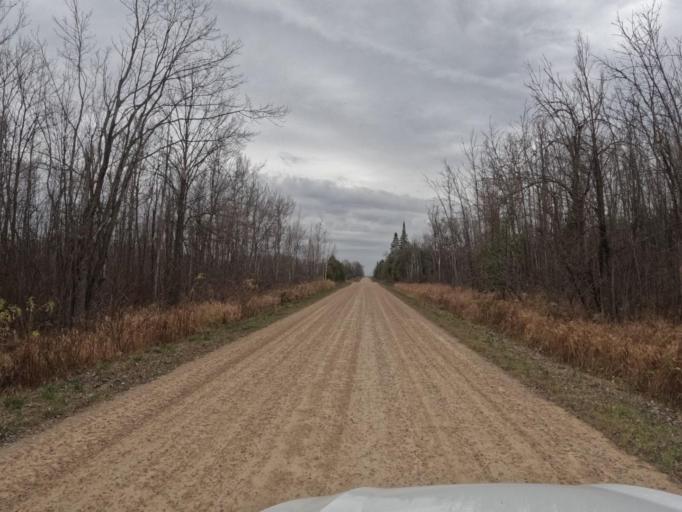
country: CA
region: Ontario
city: Shelburne
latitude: 44.0286
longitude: -80.3937
